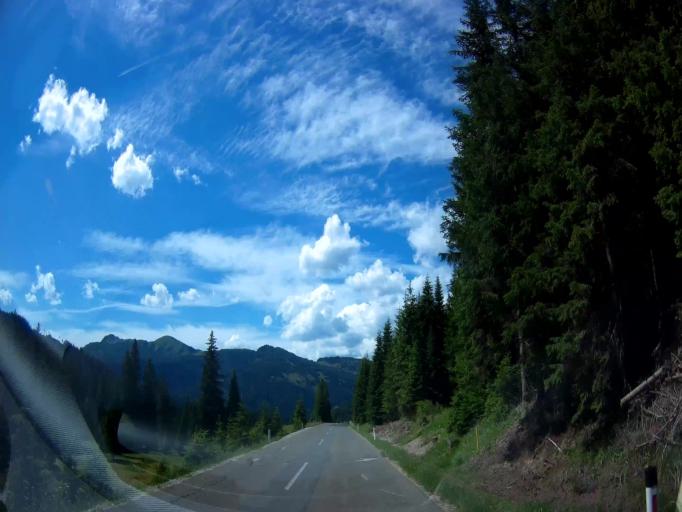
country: AT
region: Carinthia
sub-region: Politischer Bezirk Sankt Veit an der Glan
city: Glodnitz
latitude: 46.9621
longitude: 14.0234
